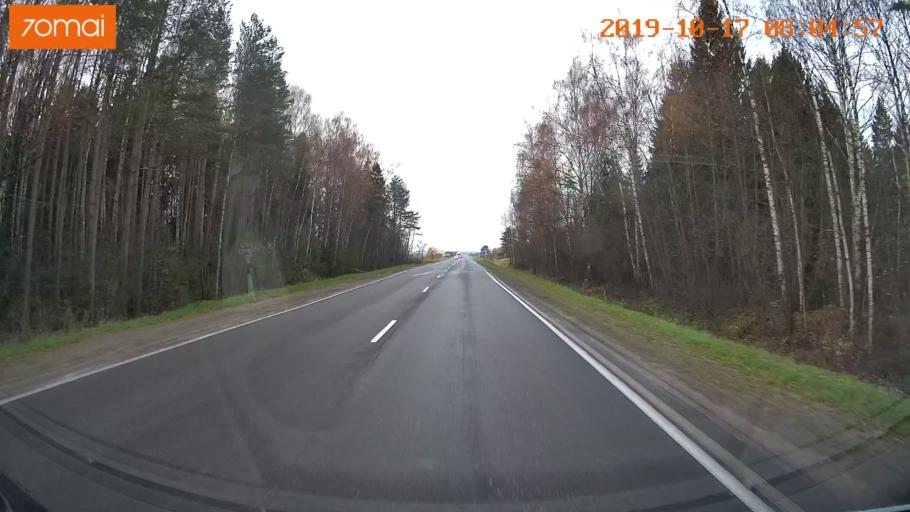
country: RU
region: Vladimir
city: Belaya Rechka
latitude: 56.3399
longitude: 39.4252
